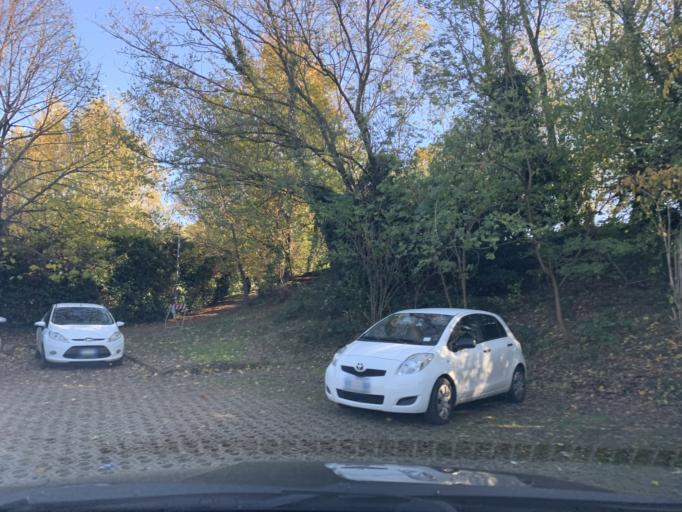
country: IT
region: Lombardy
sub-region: Provincia di Como
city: San Michele-San Giorgio
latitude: 45.6984
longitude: 9.0553
